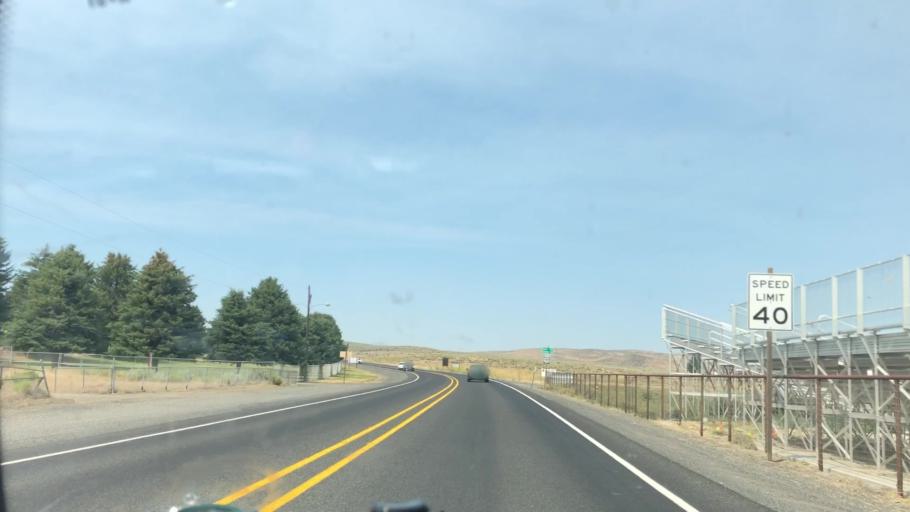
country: US
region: Idaho
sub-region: Owyhee County
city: Murphy
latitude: 42.9813
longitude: -117.0531
